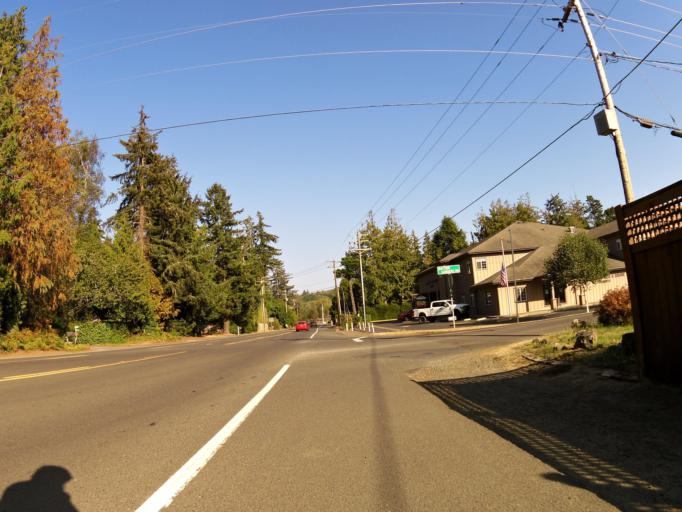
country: US
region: Oregon
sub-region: Tillamook County
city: Rockaway Beach
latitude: 45.7173
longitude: -123.9144
